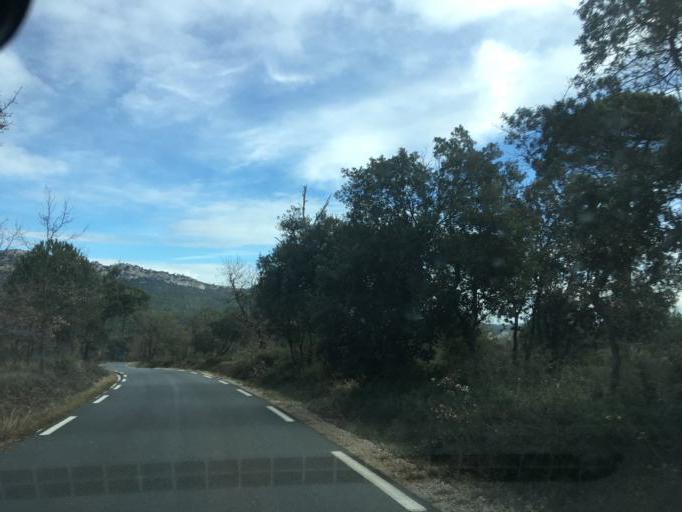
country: FR
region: Provence-Alpes-Cote d'Azur
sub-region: Departement du Var
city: Bras
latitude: 43.4471
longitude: 5.9929
